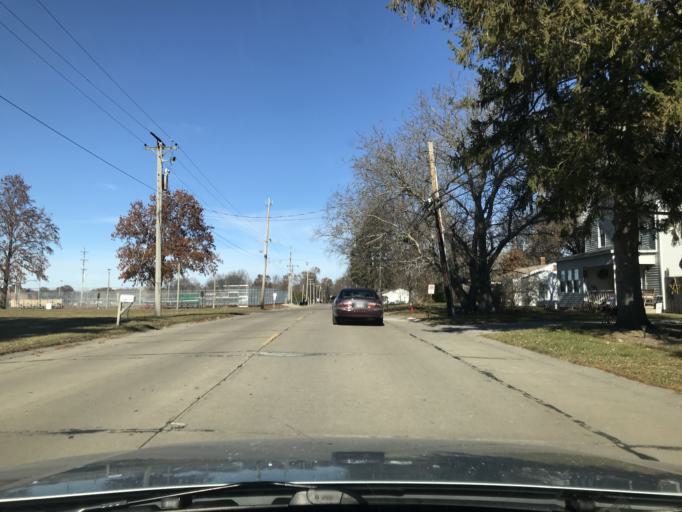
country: US
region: Illinois
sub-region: McDonough County
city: Macomb
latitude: 40.4431
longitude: -90.6708
